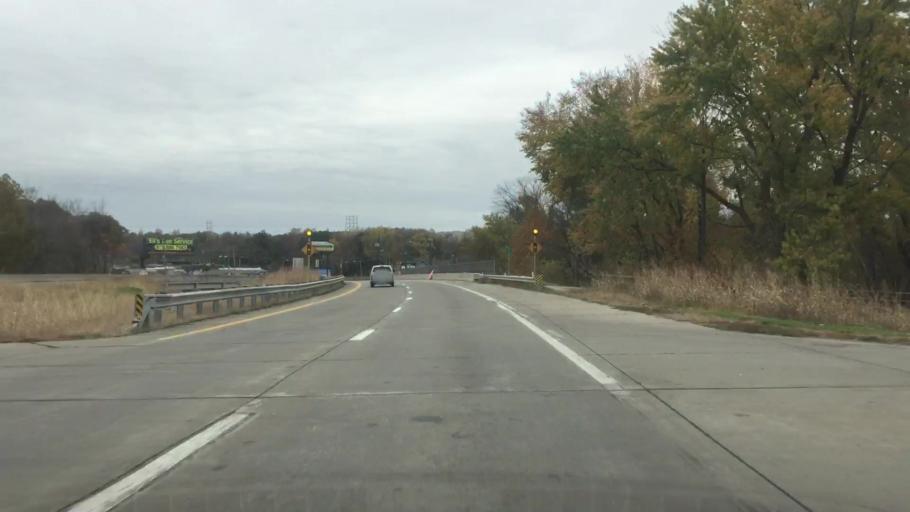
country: US
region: Missouri
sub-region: Jackson County
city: Raytown
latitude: 38.9633
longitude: -94.4259
